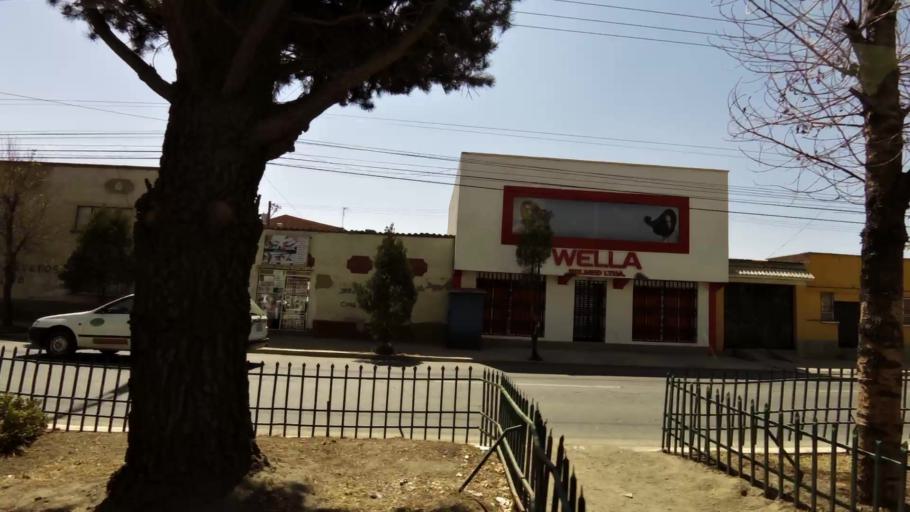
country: BO
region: La Paz
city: La Paz
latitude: -16.5248
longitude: -68.1560
